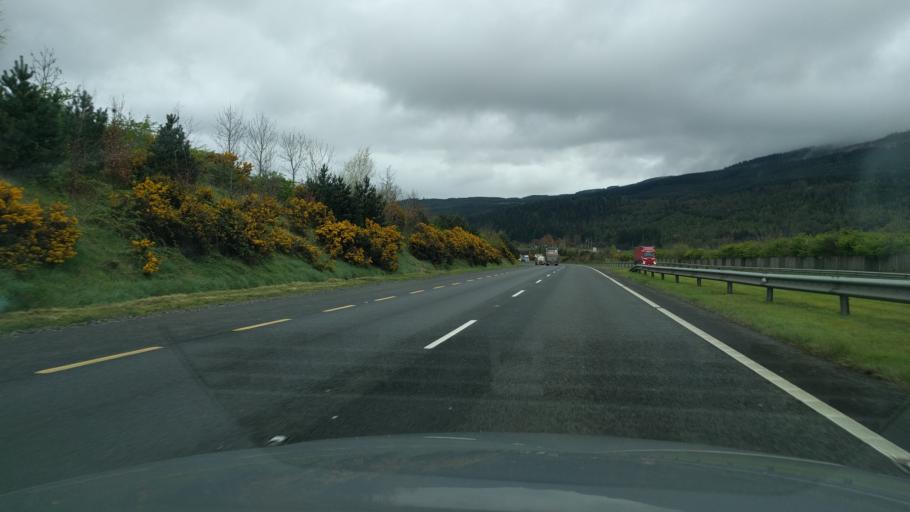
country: IE
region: Leinster
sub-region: Lu
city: Dundalk
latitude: 54.0621
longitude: -6.3547
